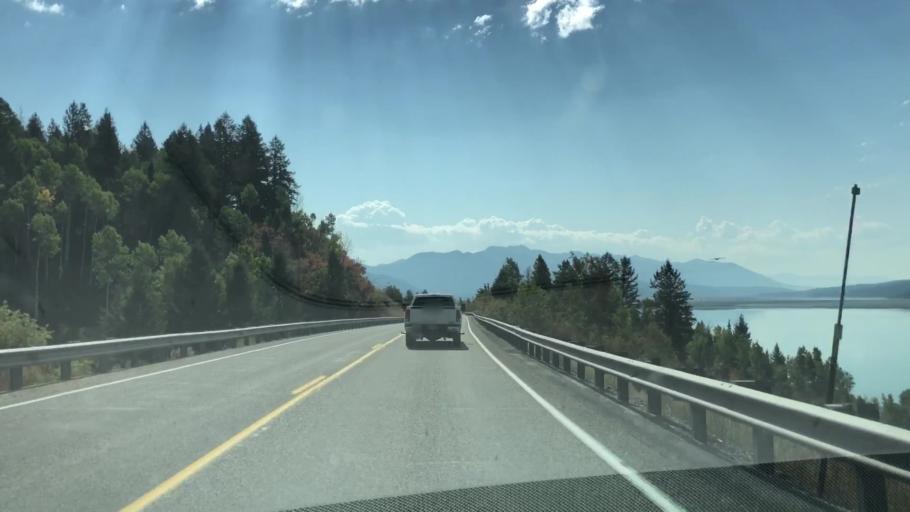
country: US
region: Wyoming
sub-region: Teton County
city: Hoback
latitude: 43.2297
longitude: -111.0888
